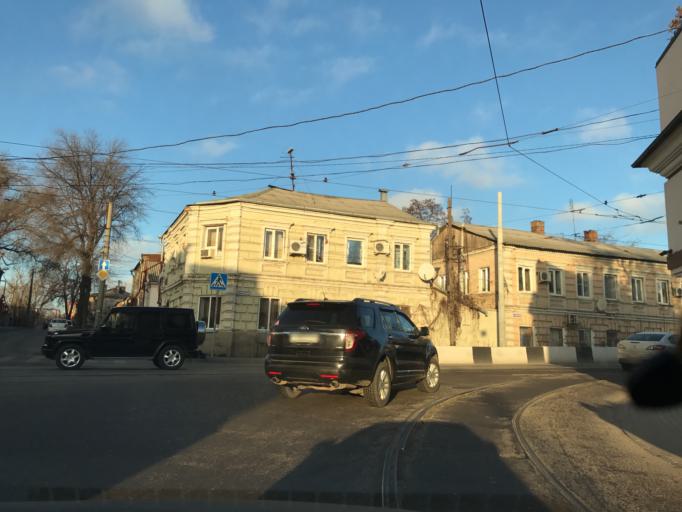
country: RU
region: Rostov
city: Rostov-na-Donu
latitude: 47.2213
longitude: 39.6854
